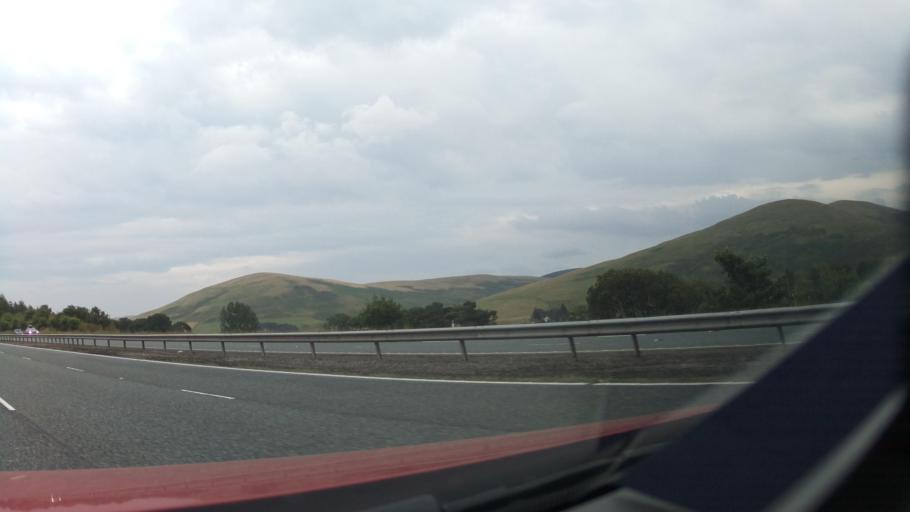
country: GB
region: Scotland
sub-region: South Lanarkshire
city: Douglas
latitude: 55.4948
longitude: -3.6957
